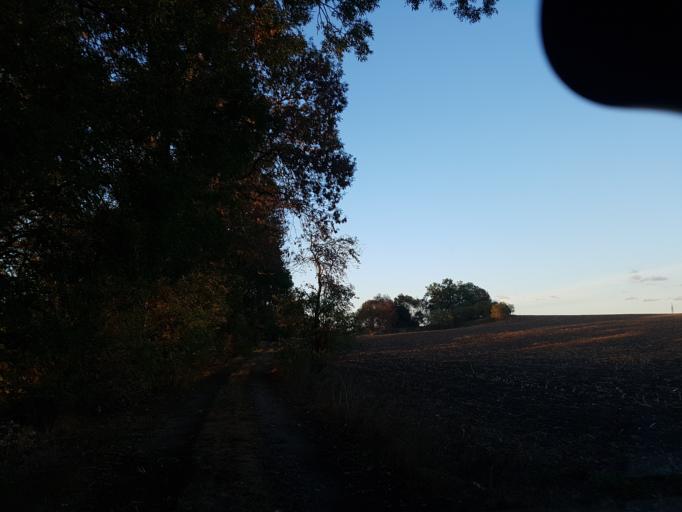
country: DE
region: Saxony
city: Oschatz
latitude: 51.2917
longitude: 13.1582
